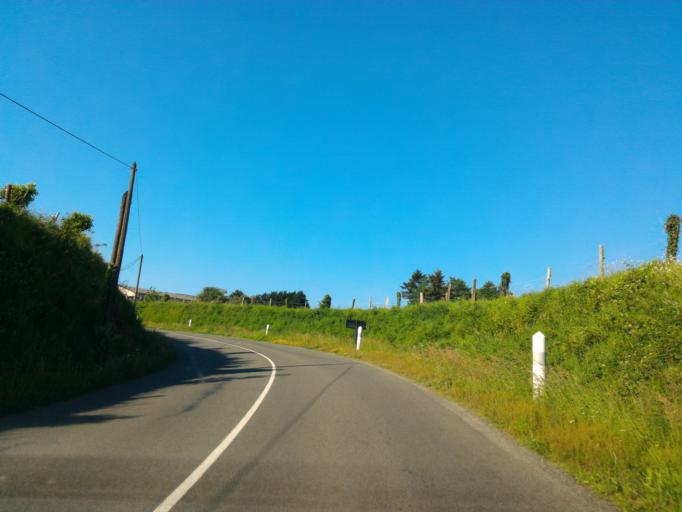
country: FR
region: Brittany
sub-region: Departement d'Ille-et-Vilaine
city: Luitre
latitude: 48.2579
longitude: -1.1269
